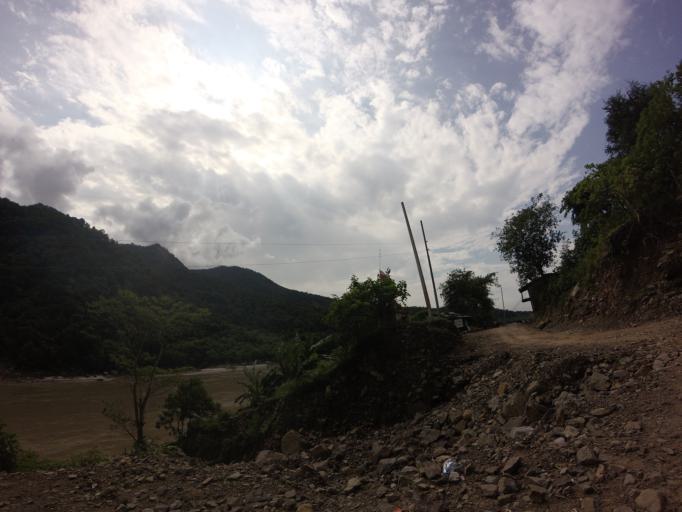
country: NP
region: Far Western
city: Tikapur
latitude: 28.6498
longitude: 81.2865
